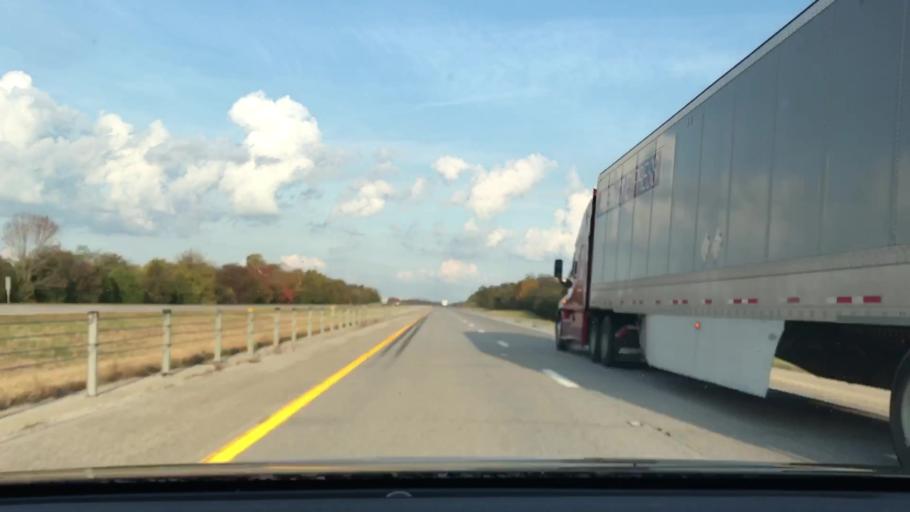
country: US
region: Kentucky
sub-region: Trigg County
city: Cadiz
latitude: 36.9117
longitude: -87.7824
